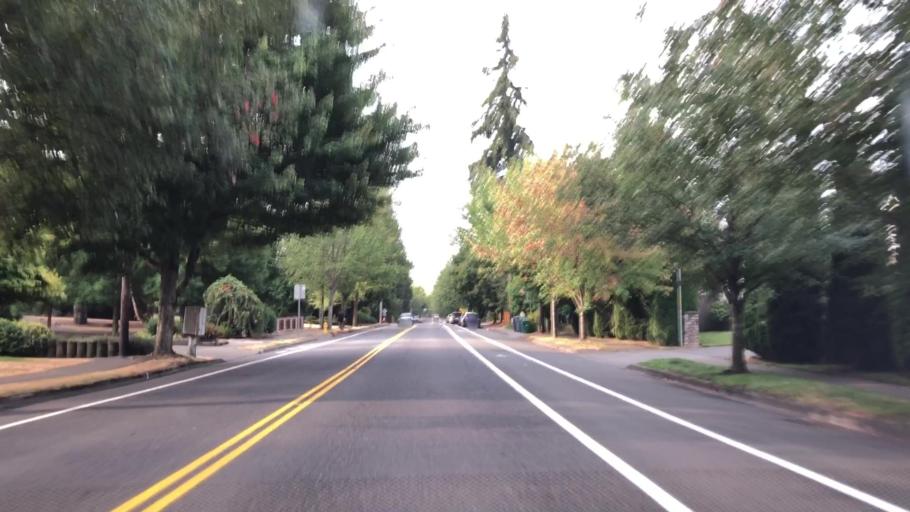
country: US
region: Washington
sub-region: King County
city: Redmond
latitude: 47.6695
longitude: -122.1640
